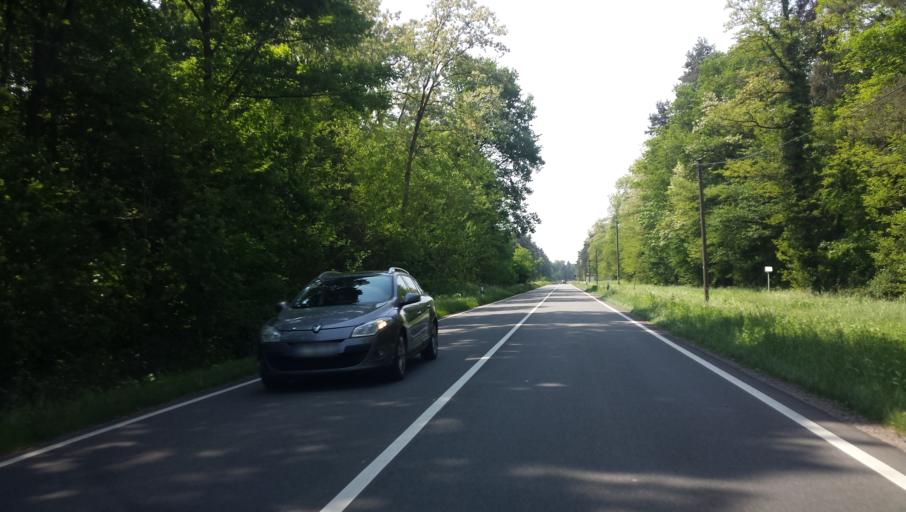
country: DE
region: Rheinland-Pfalz
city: Berg
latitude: 49.0011
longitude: 8.2156
